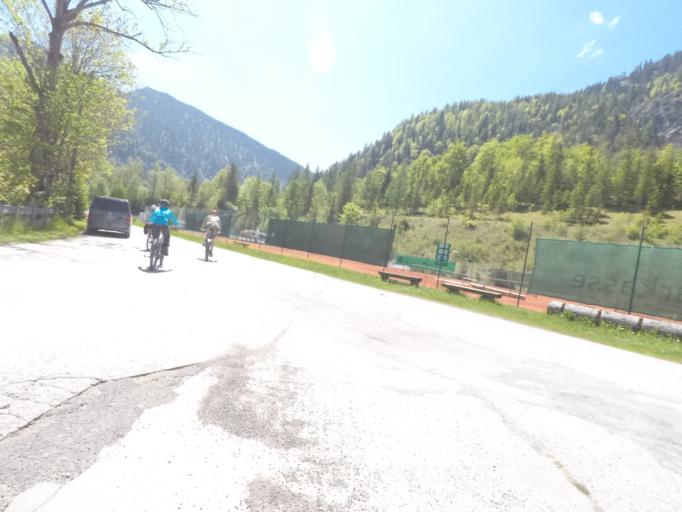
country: DE
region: Bavaria
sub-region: Upper Bavaria
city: Bayrischzell
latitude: 47.6728
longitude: 12.0085
